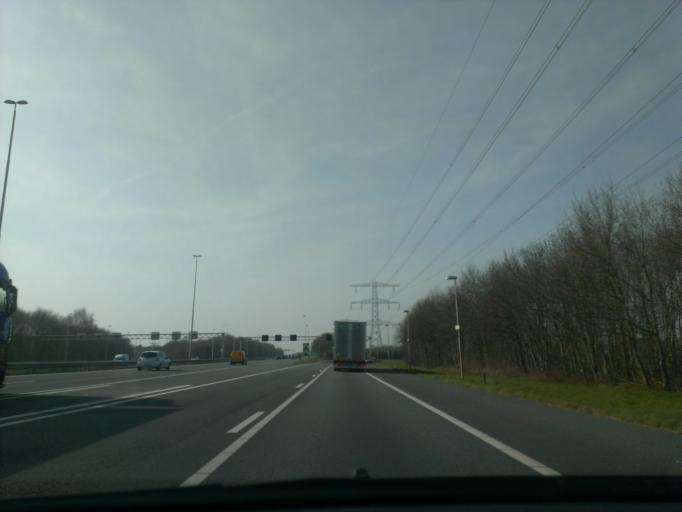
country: NL
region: Overijssel
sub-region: Gemeente Borne
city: Borne
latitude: 52.3072
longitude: 6.7061
